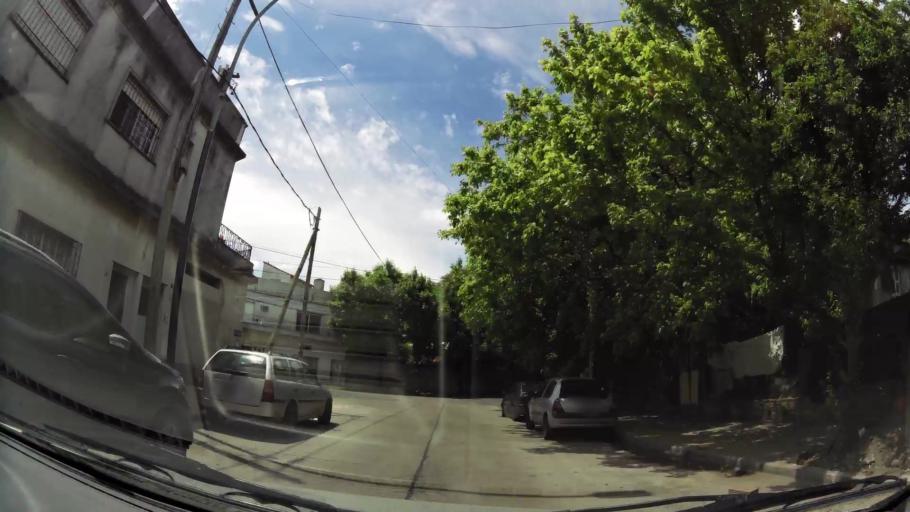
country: AR
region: Buenos Aires
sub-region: Partido de Lanus
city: Lanus
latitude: -34.6655
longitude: -58.4159
